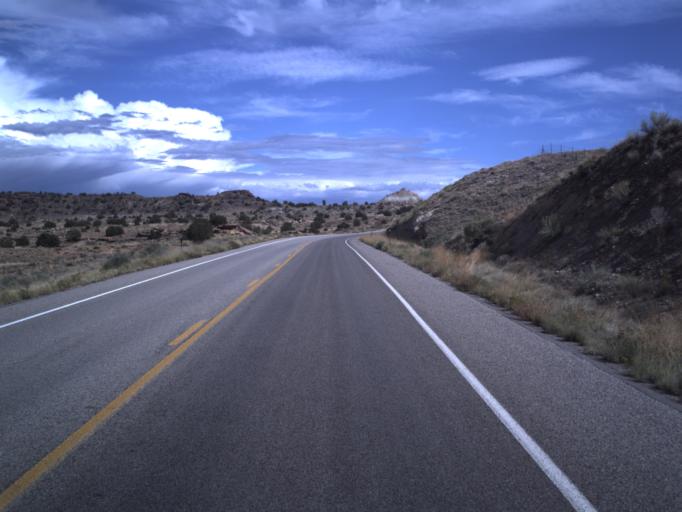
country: US
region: Colorado
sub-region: Montezuma County
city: Towaoc
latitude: 37.1945
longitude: -109.1438
